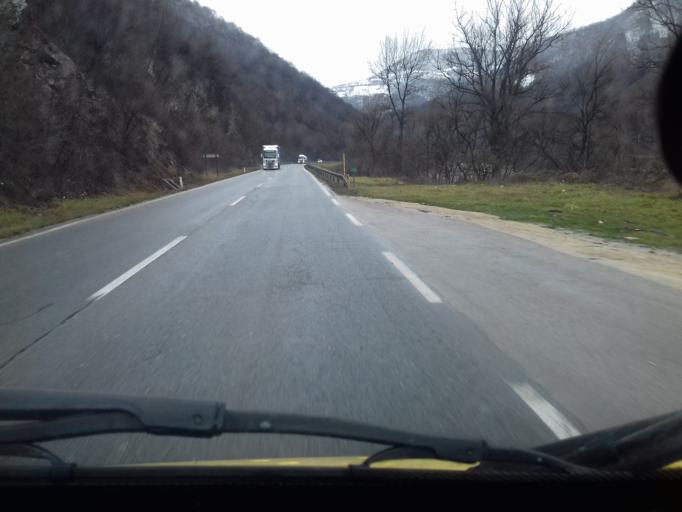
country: BA
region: Federation of Bosnia and Herzegovina
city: Lokvine
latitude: 44.2690
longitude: 17.8811
